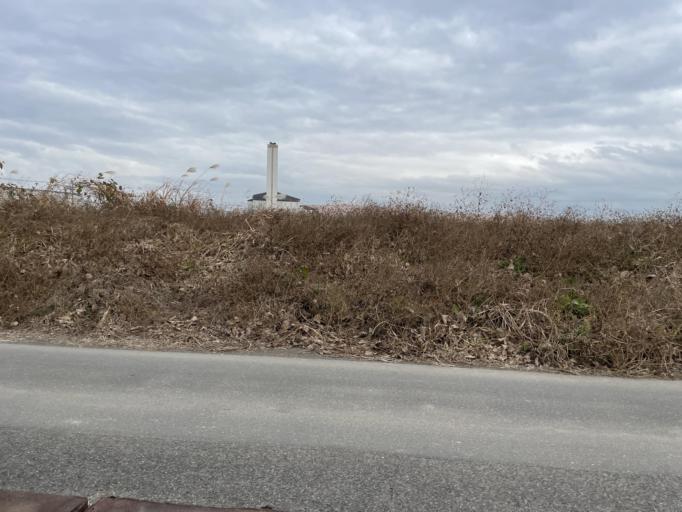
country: JP
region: Saitama
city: Shiraoka
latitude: 36.0288
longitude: 139.6447
